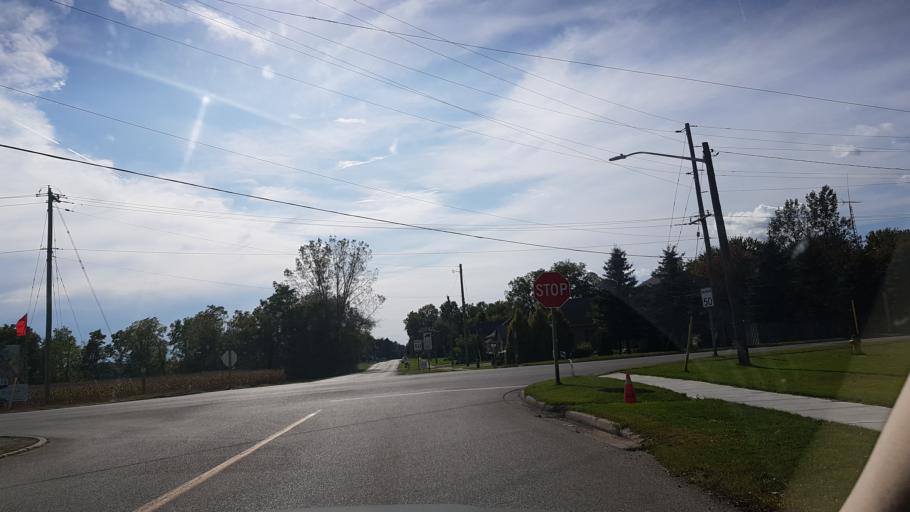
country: CA
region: Ontario
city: Delaware
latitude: 42.9026
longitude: -81.4811
